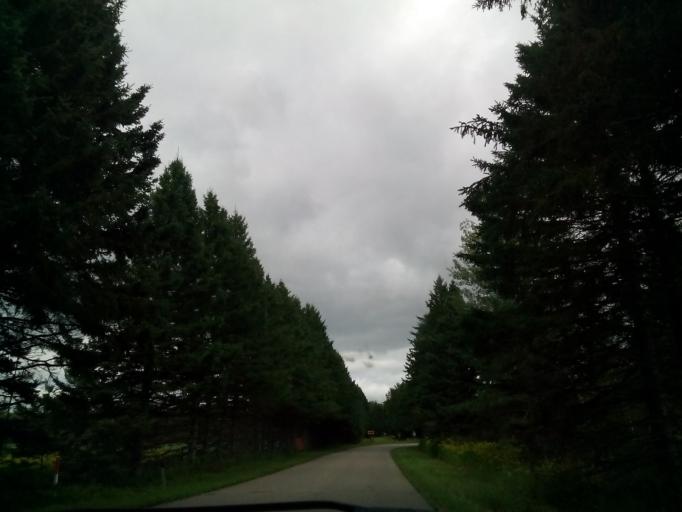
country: US
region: Wisconsin
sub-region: Menominee County
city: Legend Lake
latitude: 45.3268
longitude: -88.5298
